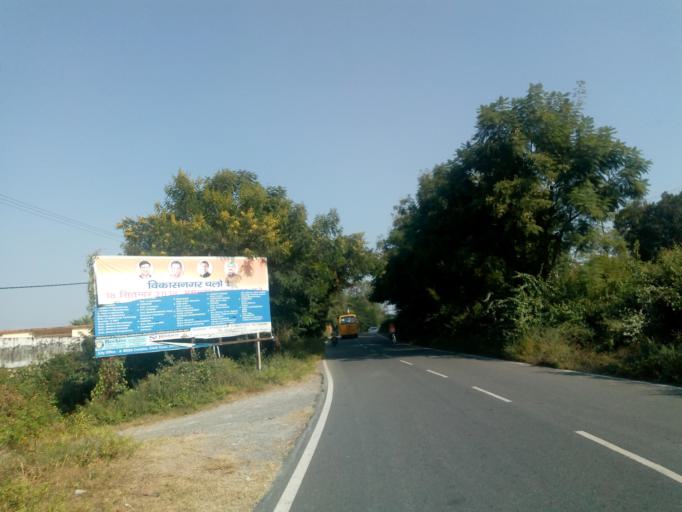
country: IN
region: Uttarakhand
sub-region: Dehradun
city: Harbatpur
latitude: 30.4416
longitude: 77.6882
